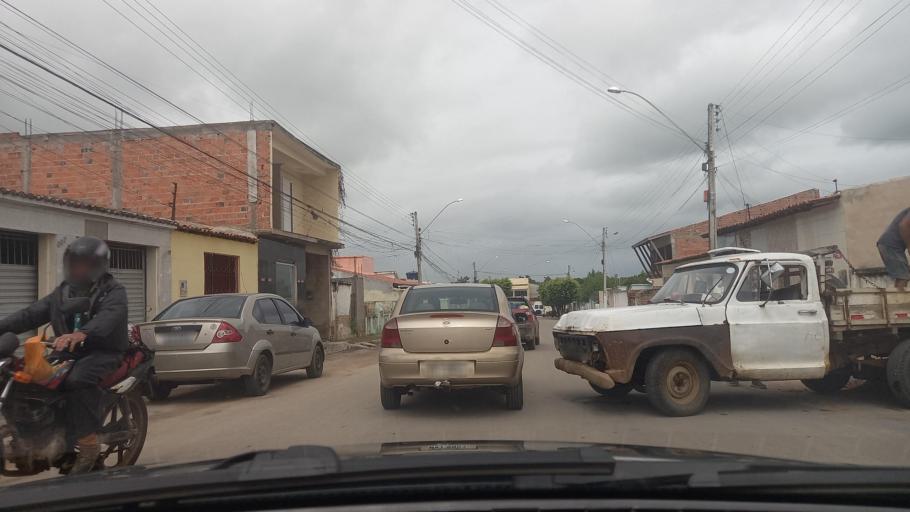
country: BR
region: Alagoas
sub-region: Delmiro Gouveia
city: Delmiro Gouveia
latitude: -9.3887
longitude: -37.9994
